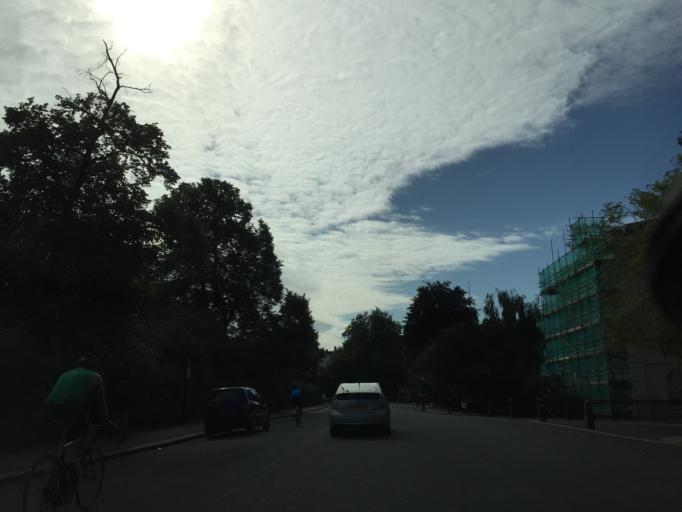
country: GB
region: England
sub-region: Greater London
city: Camden Town
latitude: 51.5259
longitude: -0.1596
